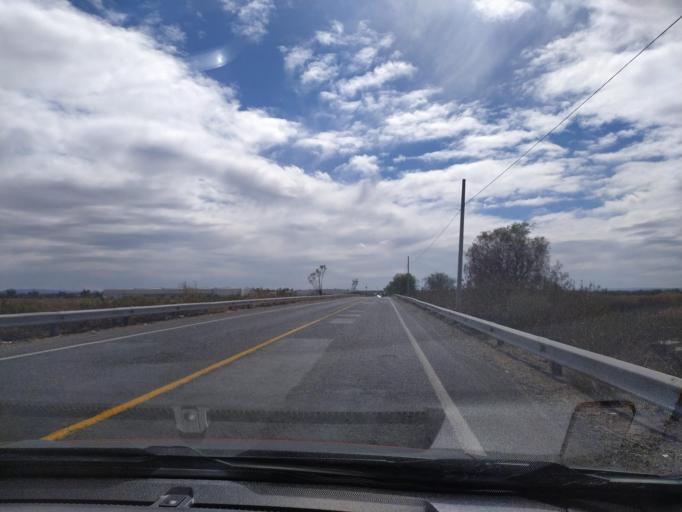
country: LA
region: Oudomxai
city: Muang La
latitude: 21.0101
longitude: 101.8292
